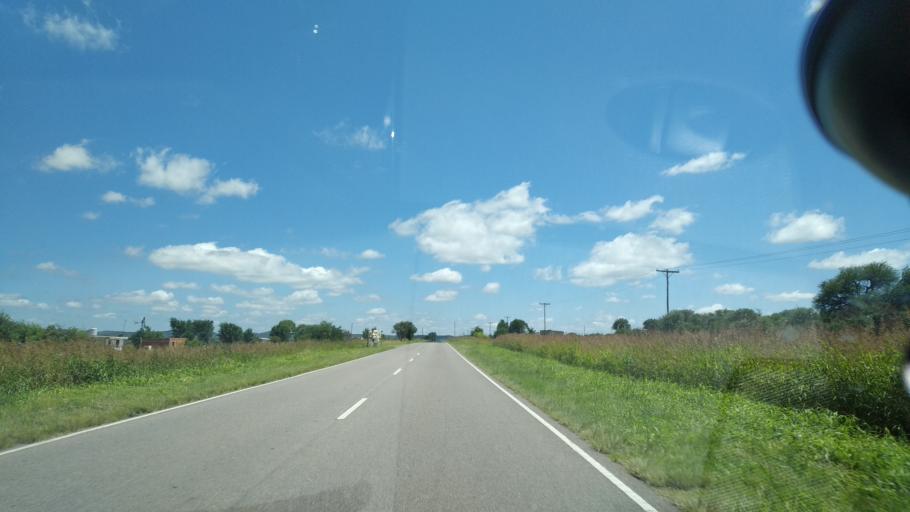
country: AR
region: Cordoba
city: Salsacate
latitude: -31.3961
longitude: -65.0978
